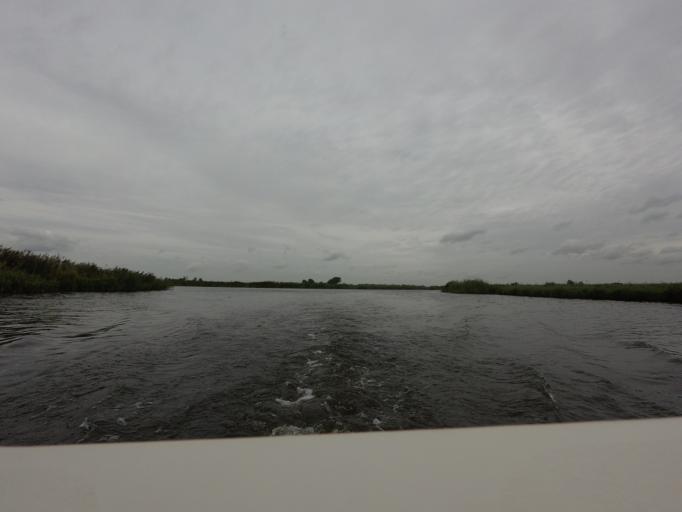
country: NL
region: Friesland
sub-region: Gemeente Boarnsterhim
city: Warten
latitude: 53.1166
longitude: 5.8864
